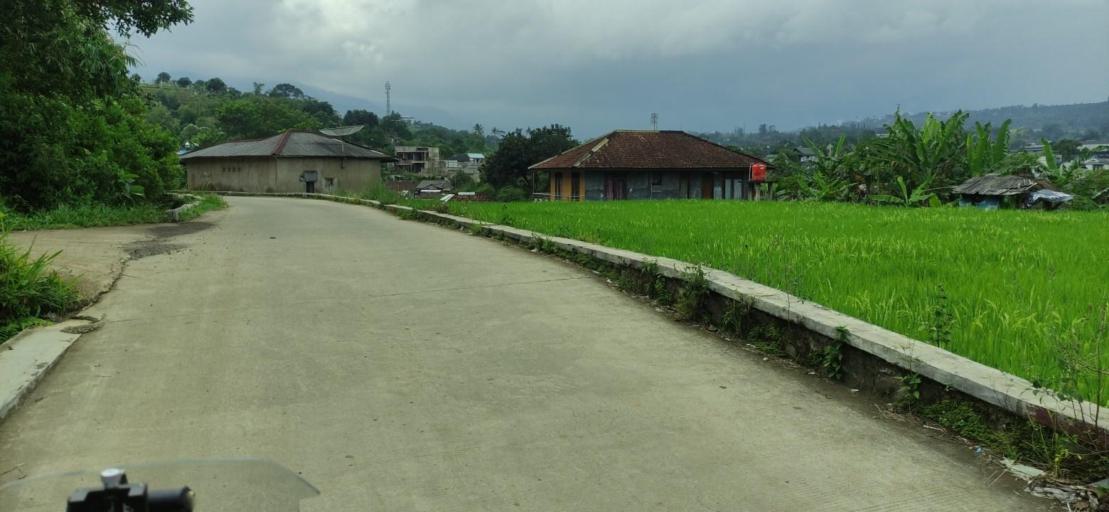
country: ID
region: West Java
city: Caringin
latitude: -6.6435
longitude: 106.8985
